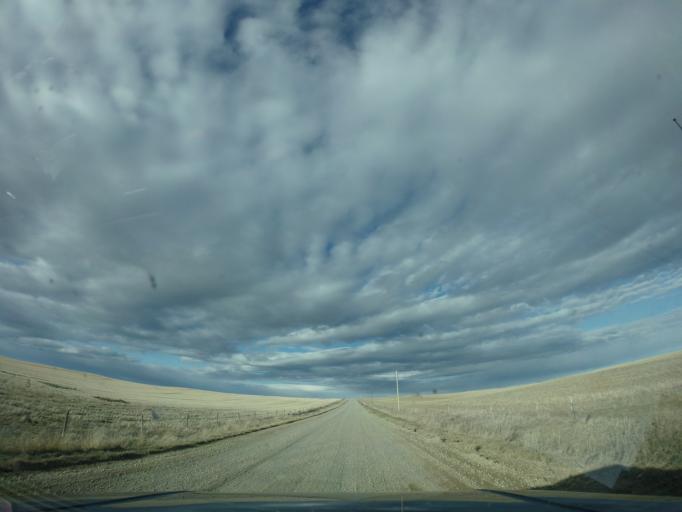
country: US
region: Montana
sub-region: Yellowstone County
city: Laurel
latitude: 45.8959
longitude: -108.8810
